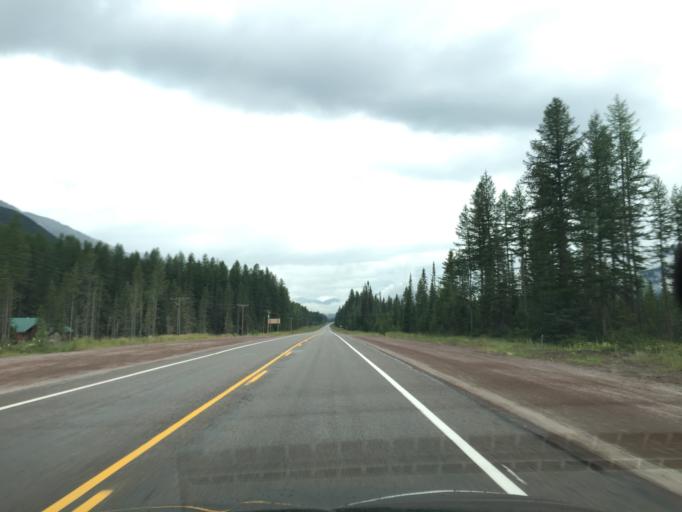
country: US
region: Montana
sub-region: Flathead County
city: Bigfork
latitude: 48.2859
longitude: -113.6078
